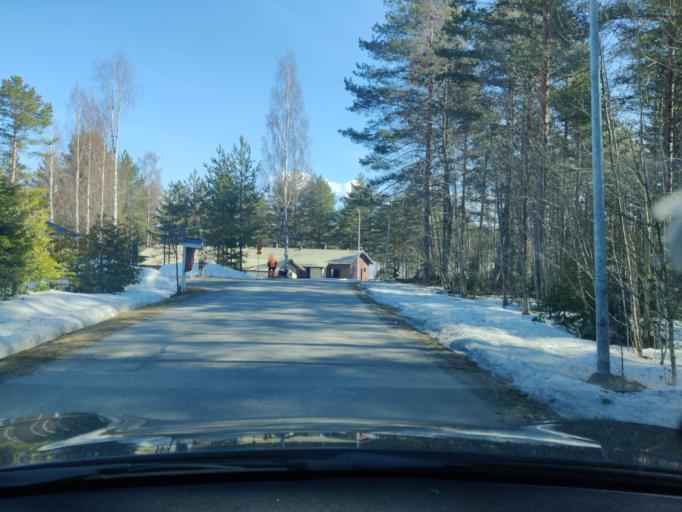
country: FI
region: Northern Savo
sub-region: Kuopio
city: Vehmersalmi
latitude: 62.7699
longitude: 27.9901
